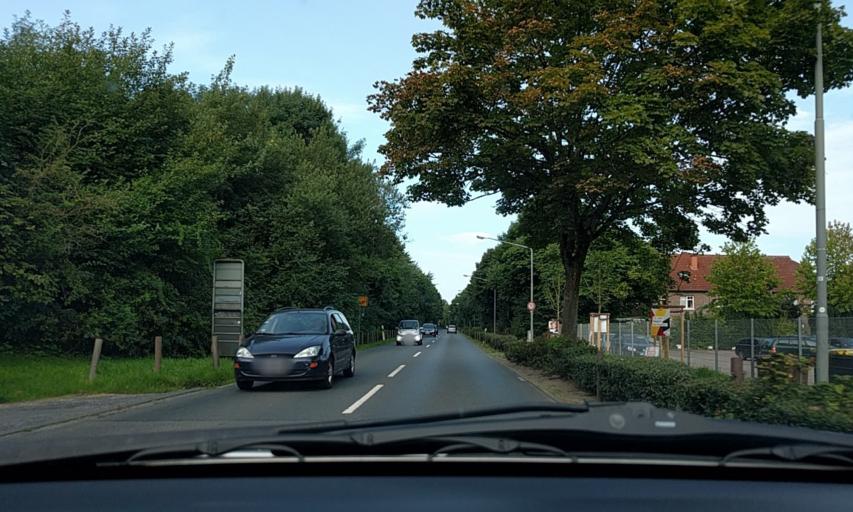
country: DE
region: North Rhine-Westphalia
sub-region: Regierungsbezirk Dusseldorf
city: Ratingen
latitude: 51.2885
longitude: 6.8254
